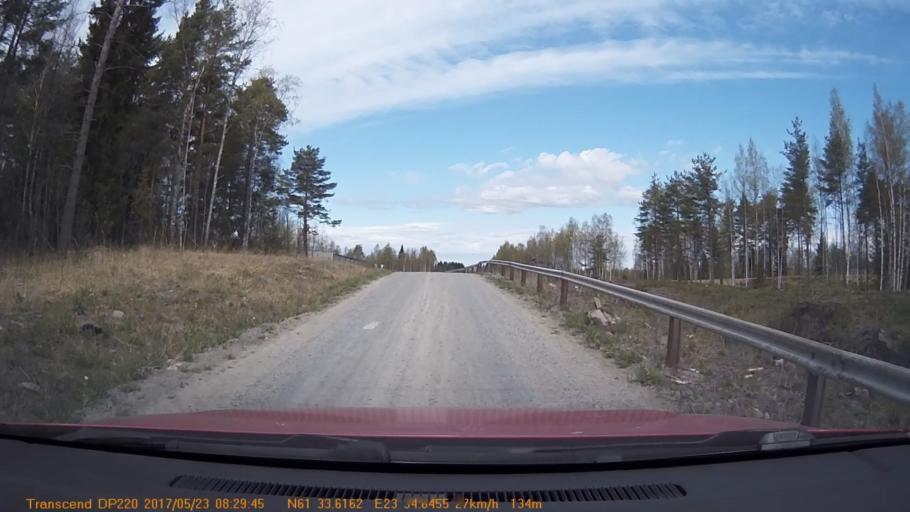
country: FI
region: Pirkanmaa
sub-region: Tampere
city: Yloejaervi
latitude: 61.5602
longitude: 23.5773
